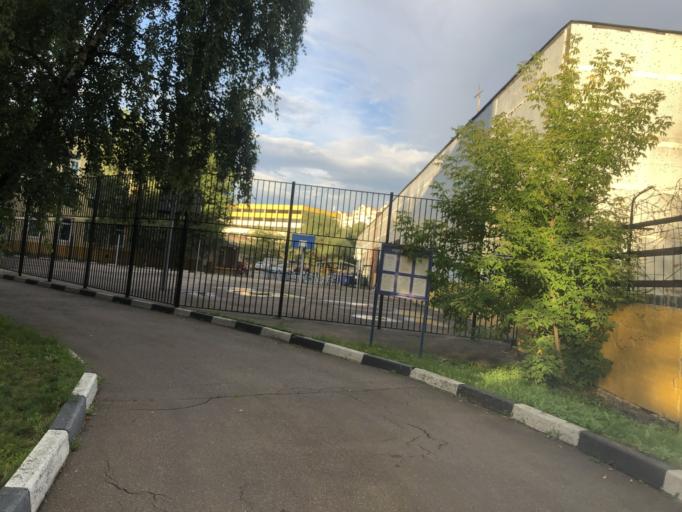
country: RU
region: Moskovskaya
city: Bol'shaya Setun'
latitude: 55.7369
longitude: 37.3949
